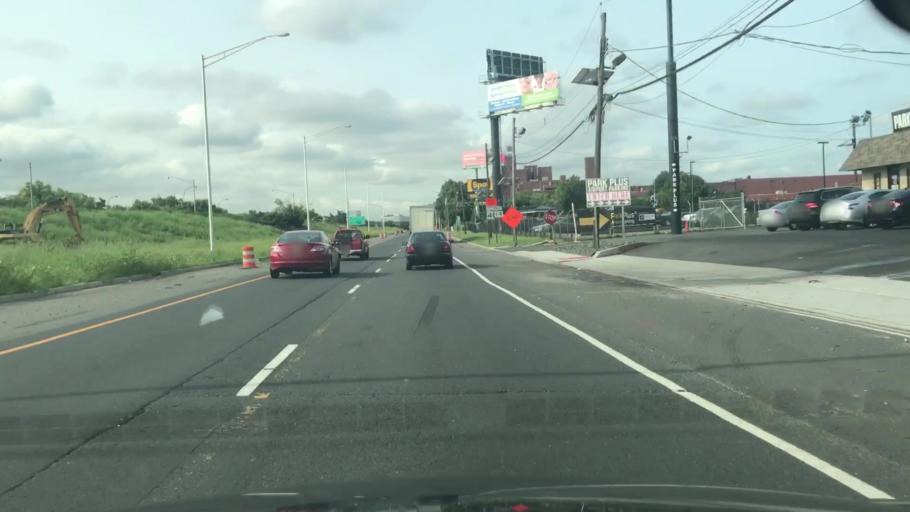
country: US
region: New Jersey
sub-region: Essex County
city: Newark
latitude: 40.6985
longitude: -74.1873
